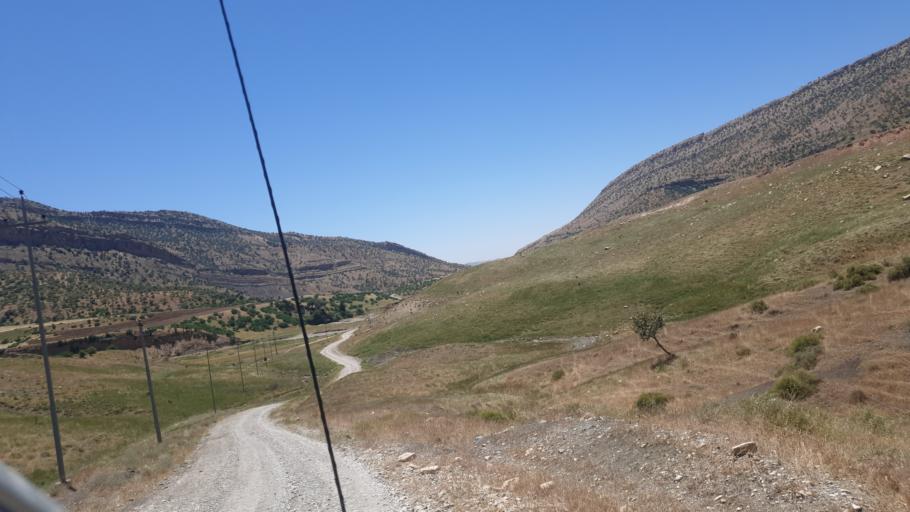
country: IQ
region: Arbil
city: Nahiyat Hiran
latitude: 36.1982
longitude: 44.4221
